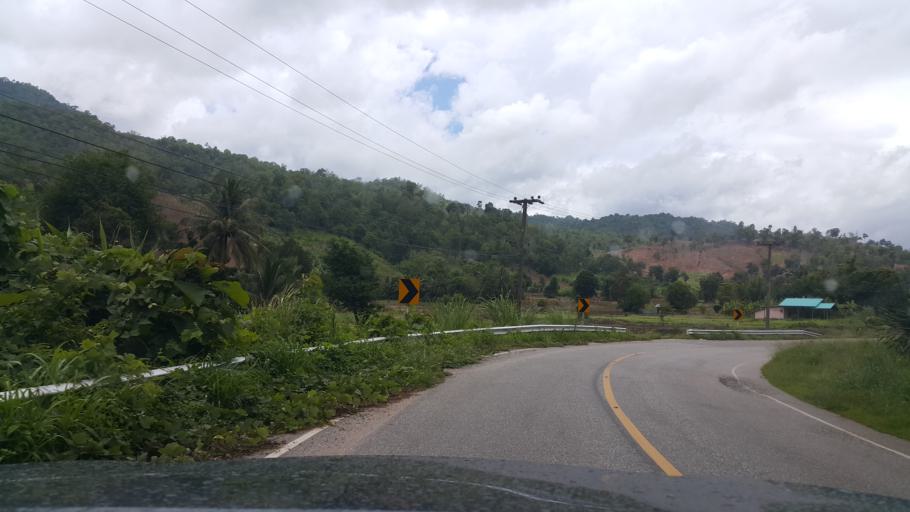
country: TH
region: Loei
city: Na Haeo
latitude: 17.5357
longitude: 100.8328
